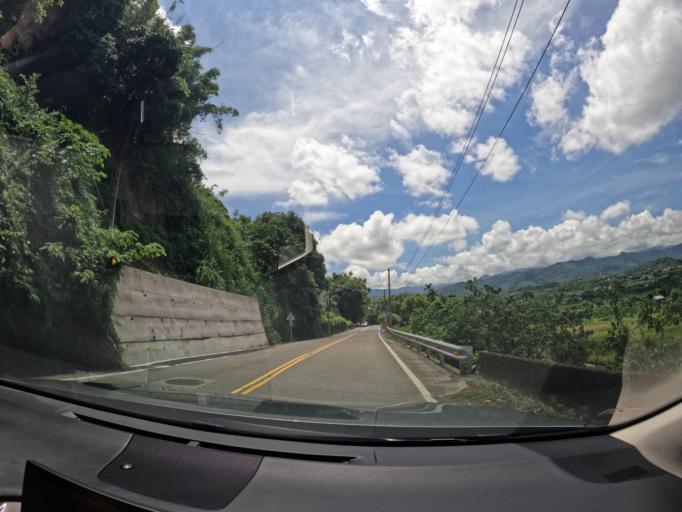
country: TW
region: Taiwan
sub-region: Hsinchu
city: Hsinchu
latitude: 24.6471
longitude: 120.9606
